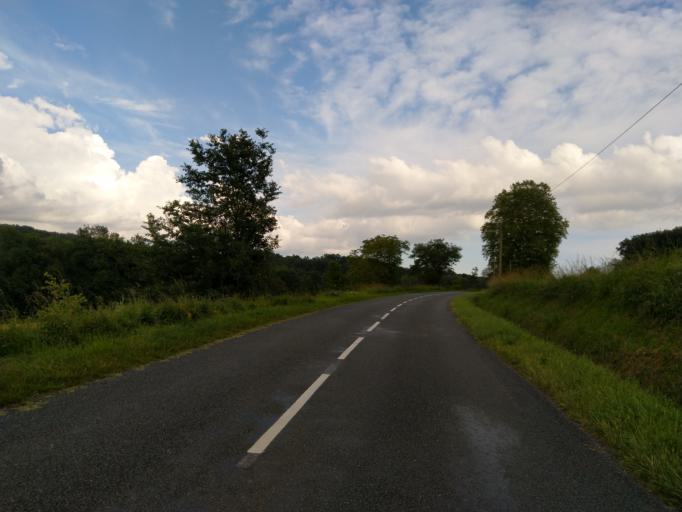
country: FR
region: Midi-Pyrenees
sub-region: Departement du Tarn
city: Realmont
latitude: 43.7991
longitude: 2.1593
